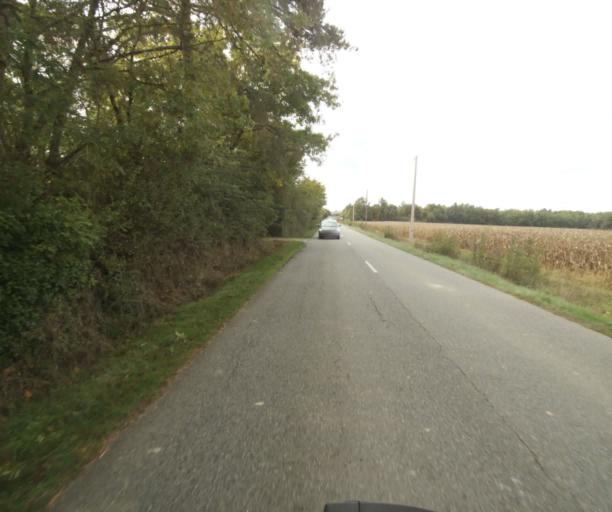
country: FR
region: Midi-Pyrenees
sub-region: Departement du Tarn-et-Garonne
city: Verdun-sur-Garonne
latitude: 43.8498
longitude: 1.1427
